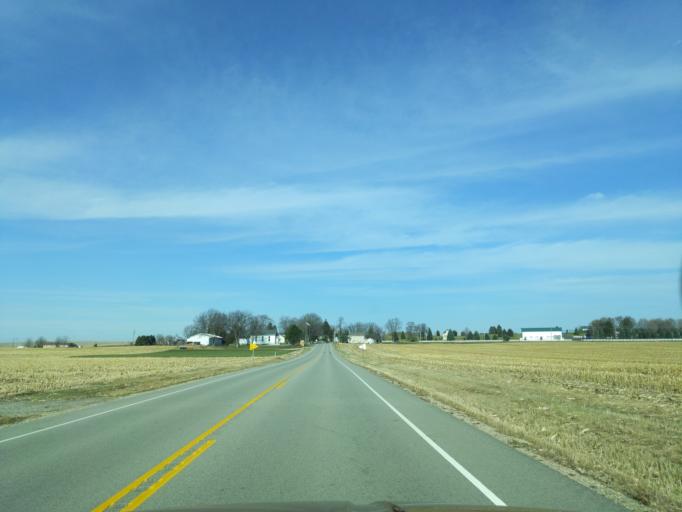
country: US
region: Wisconsin
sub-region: Walworth County
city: Elkhorn
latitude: 42.7298
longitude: -88.5821
